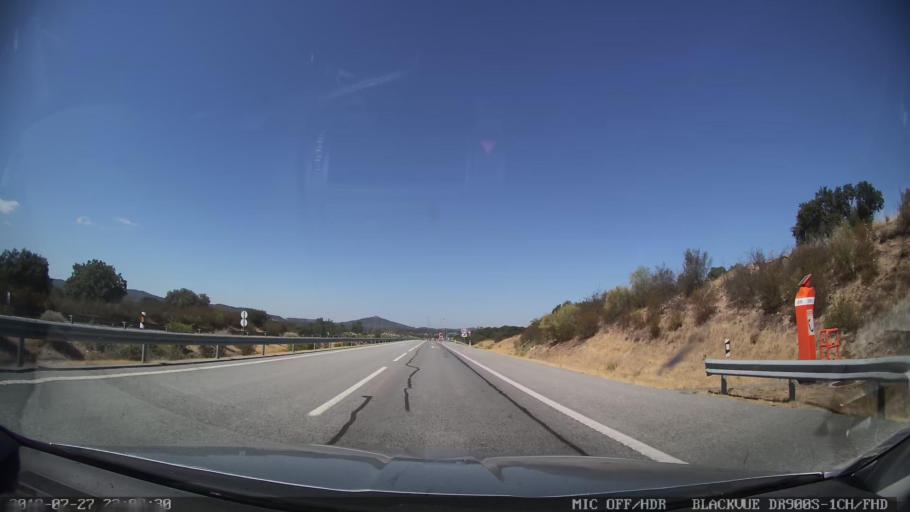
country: PT
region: Evora
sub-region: Estremoz
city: Estremoz
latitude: 38.8019
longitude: -7.6548
